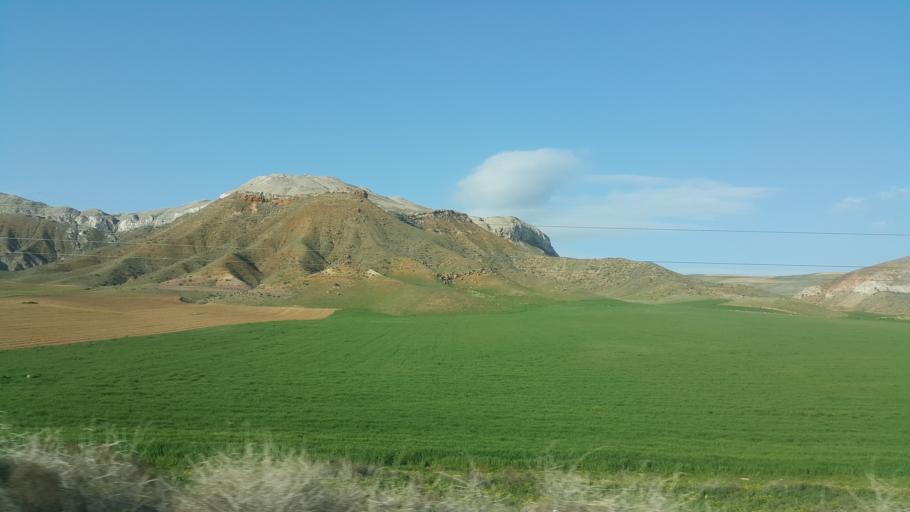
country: TR
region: Ankara
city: Sereflikochisar
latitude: 38.9910
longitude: 33.4744
